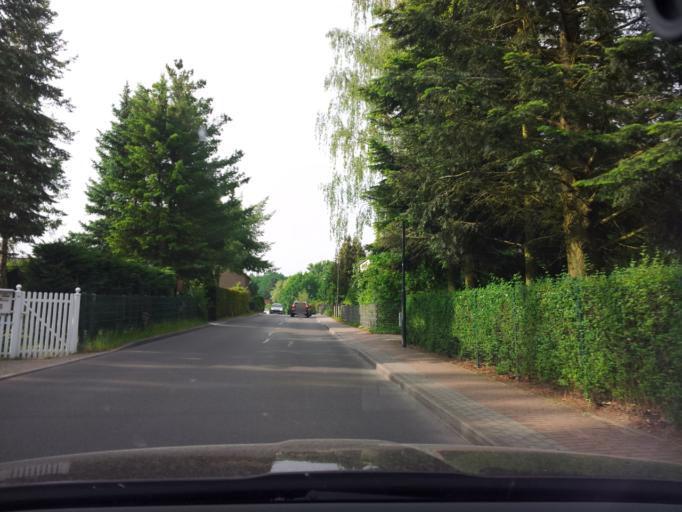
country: DE
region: Brandenburg
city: Werder
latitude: 52.3227
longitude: 12.9270
